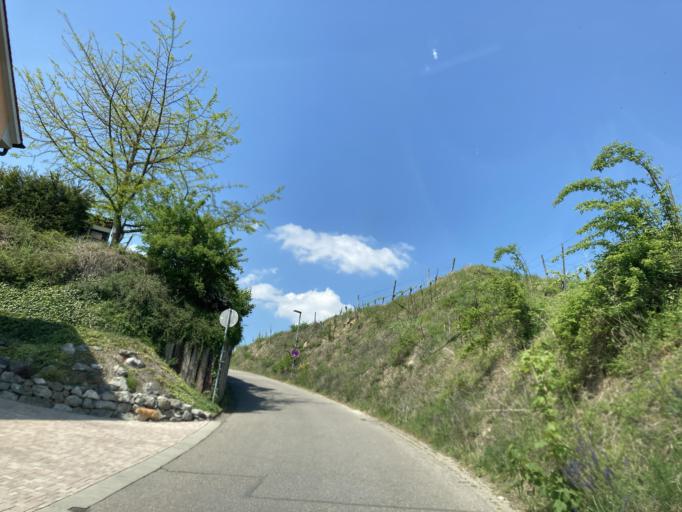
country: DE
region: Baden-Wuerttemberg
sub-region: Freiburg Region
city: Sasbach
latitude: 48.1024
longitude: 7.5988
